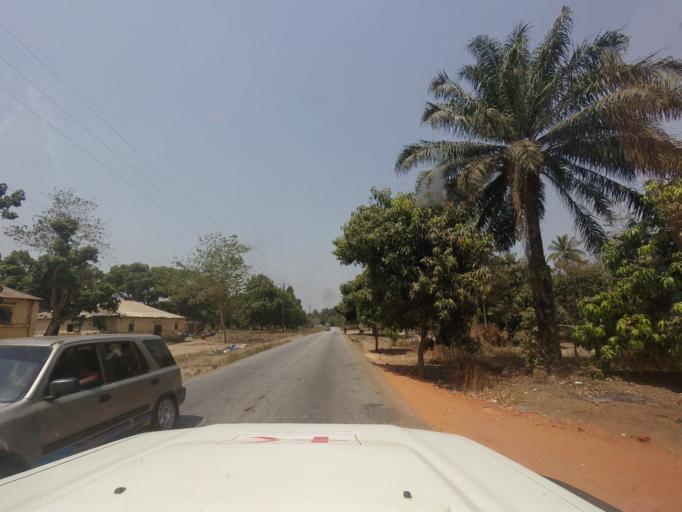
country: GN
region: Kindia
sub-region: Kindia
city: Kindia
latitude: 9.9597
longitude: -12.9414
